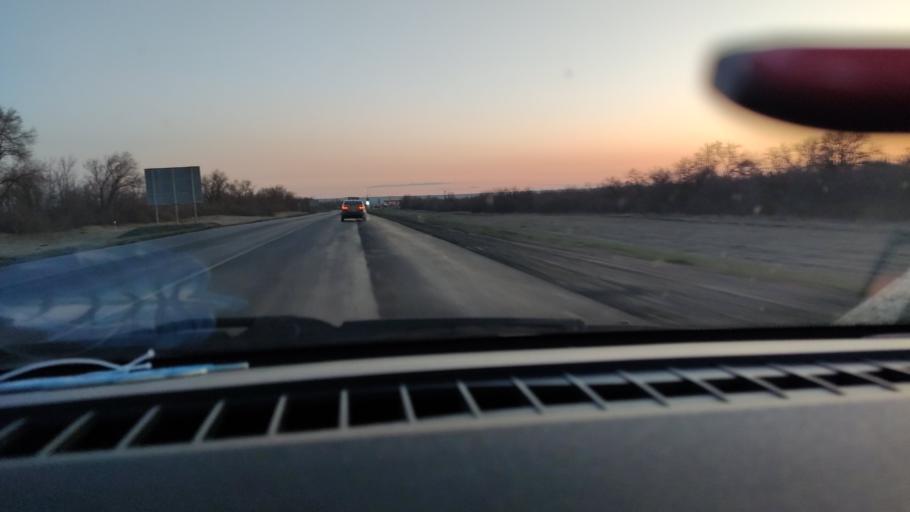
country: RU
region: Saratov
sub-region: Saratovskiy Rayon
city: Saratov
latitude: 51.6765
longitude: 46.0010
